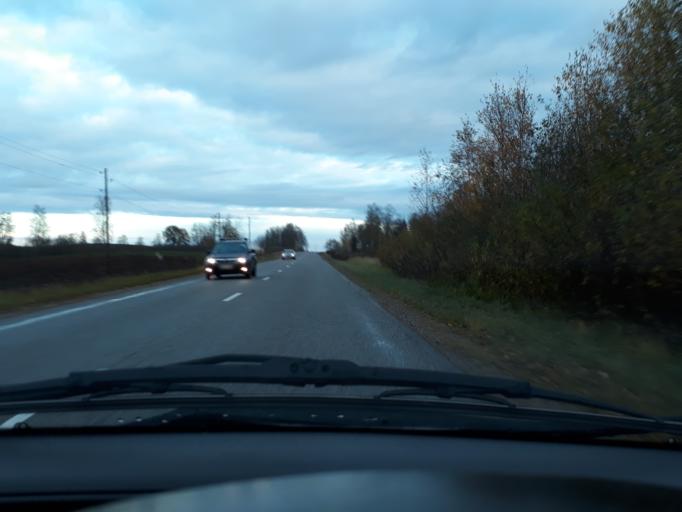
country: LV
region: Dobeles Rajons
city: Dobele
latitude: 56.5942
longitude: 23.1391
